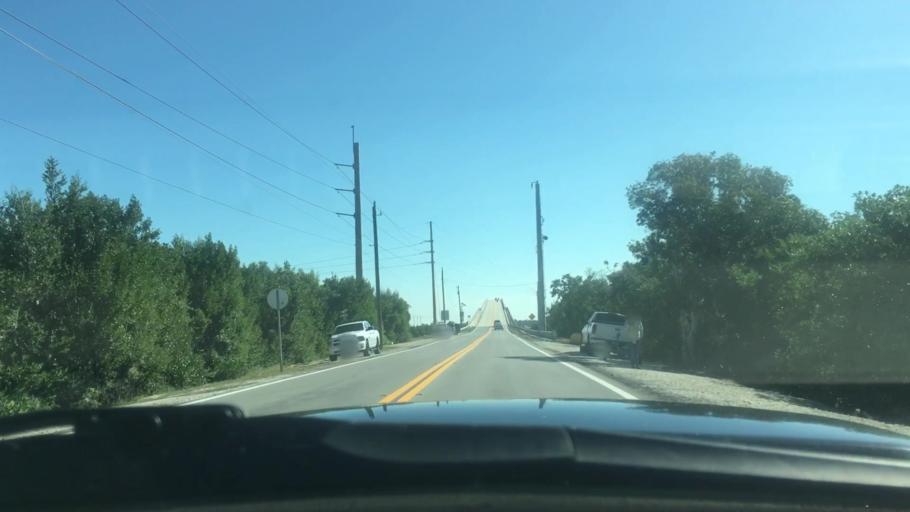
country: US
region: Florida
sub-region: Monroe County
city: North Key Largo
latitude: 25.2897
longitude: -80.3743
